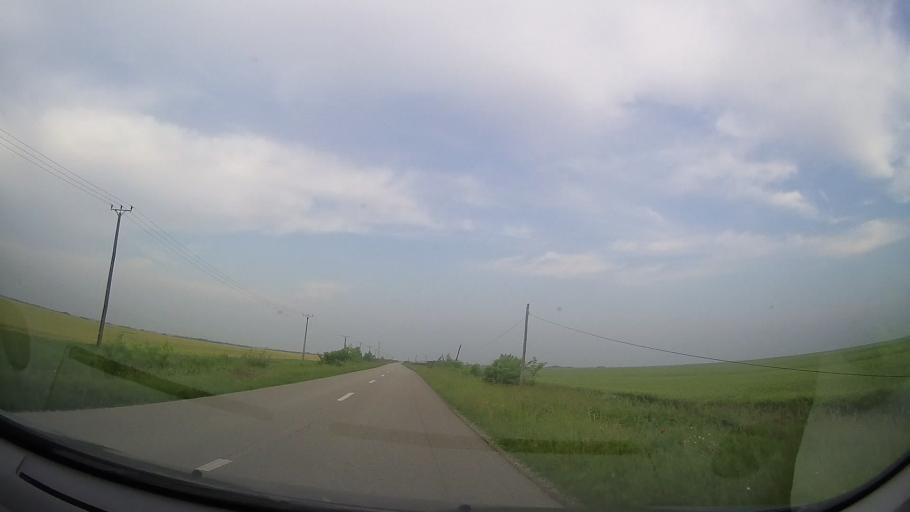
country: RO
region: Timis
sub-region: Comuna Foeni
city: Foeni
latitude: 45.5201
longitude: 20.9080
